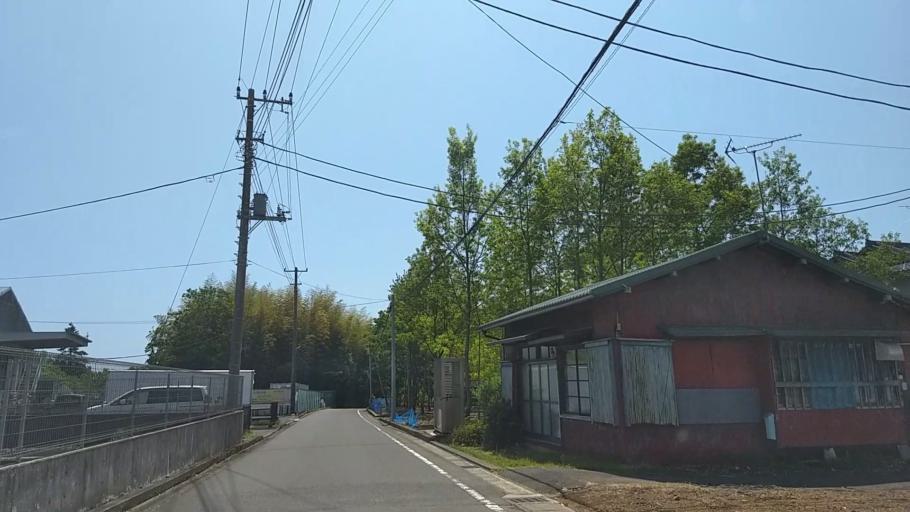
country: JP
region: Shizuoka
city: Mishima
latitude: 35.2043
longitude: 138.9094
